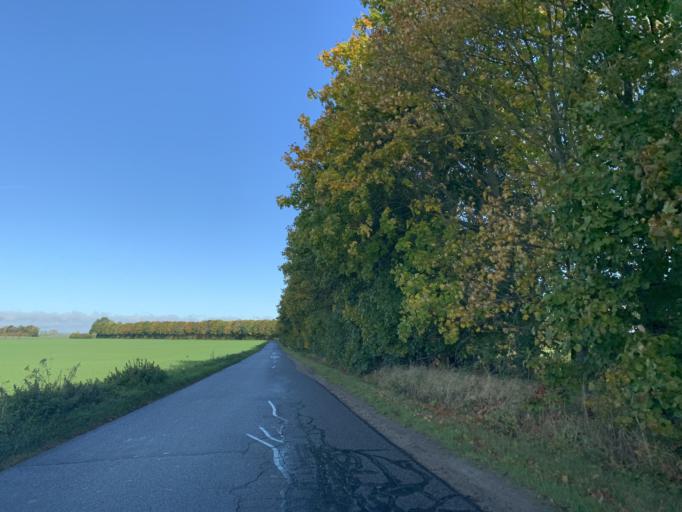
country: DE
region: Mecklenburg-Vorpommern
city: Gross Nemerow
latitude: 53.4697
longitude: 13.2705
